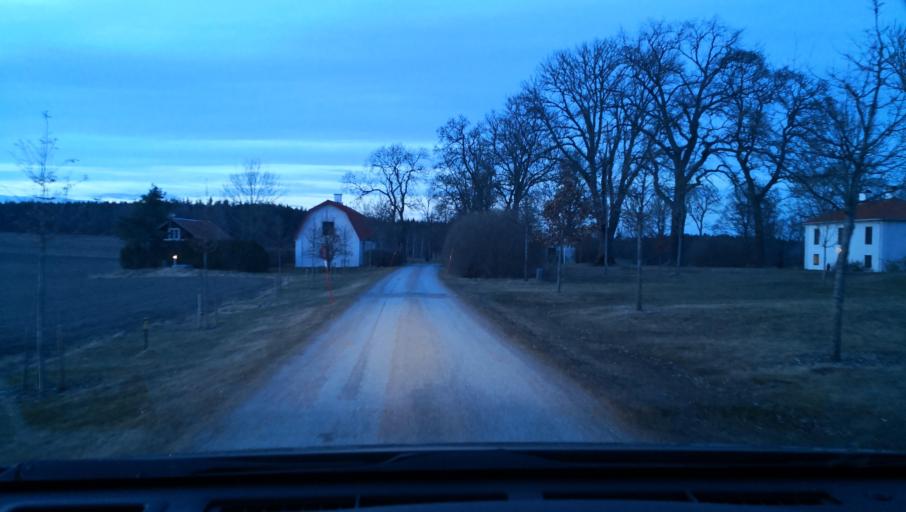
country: SE
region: Uppsala
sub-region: Enkopings Kommun
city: Dalby
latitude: 59.5561
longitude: 17.3707
